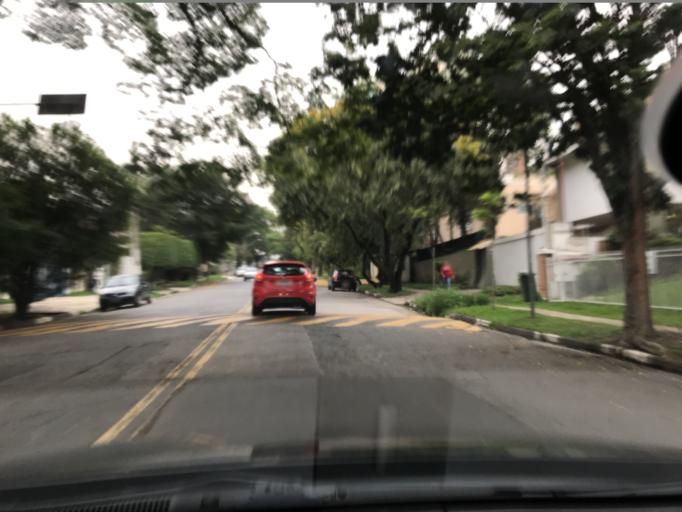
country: BR
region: Sao Paulo
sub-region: Sao Paulo
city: Sao Paulo
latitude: -23.5512
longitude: -46.7021
